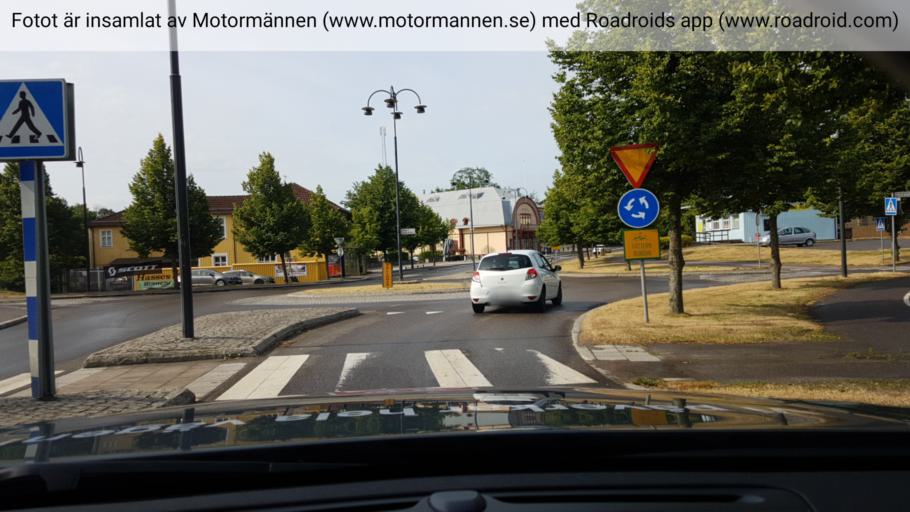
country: SE
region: OEstergoetland
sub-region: Motala Kommun
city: Motala
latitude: 58.5492
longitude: 15.0621
